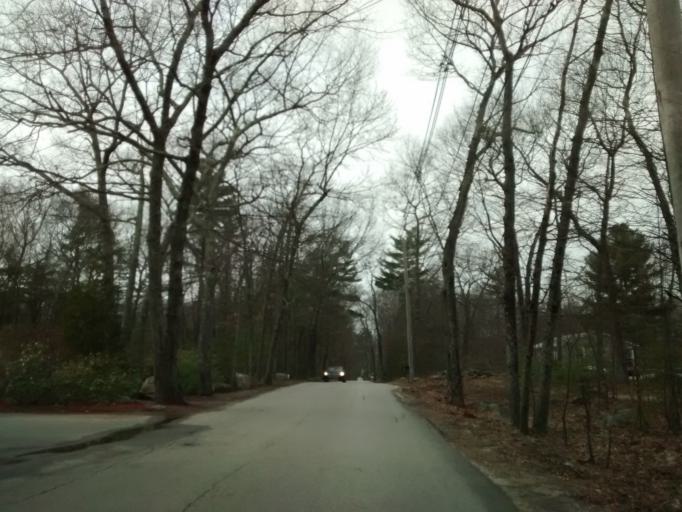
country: US
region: Massachusetts
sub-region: Worcester County
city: Douglas
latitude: 42.0463
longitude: -71.7260
